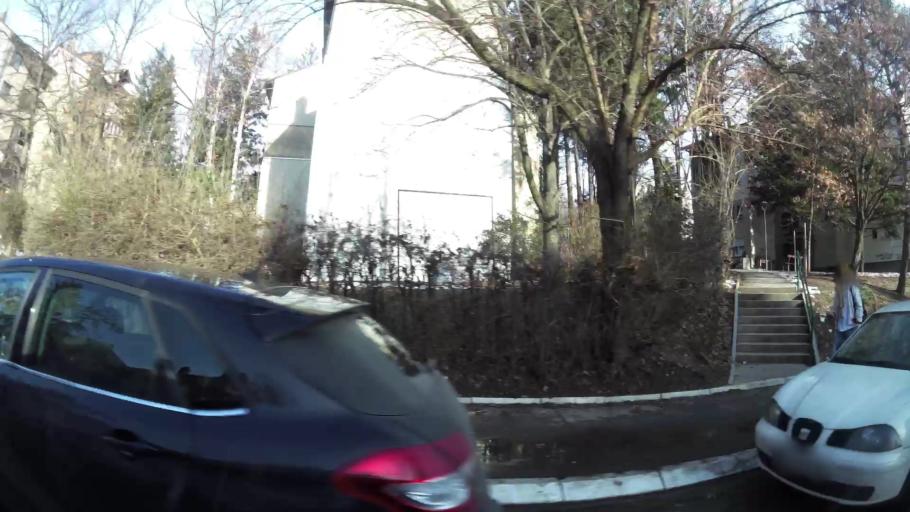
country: RS
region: Central Serbia
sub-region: Belgrade
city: Rakovica
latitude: 44.7250
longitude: 20.4274
